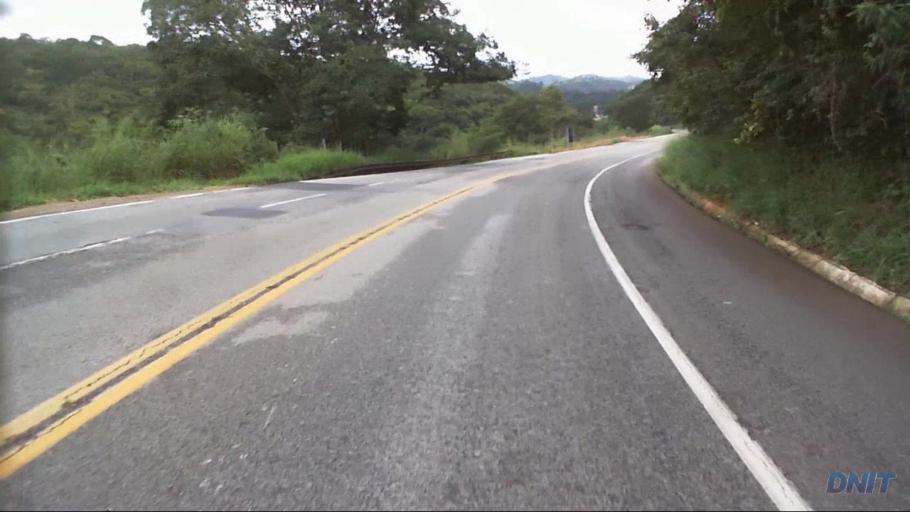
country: BR
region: Minas Gerais
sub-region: Joao Monlevade
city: Joao Monlevade
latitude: -19.8387
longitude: -43.3417
